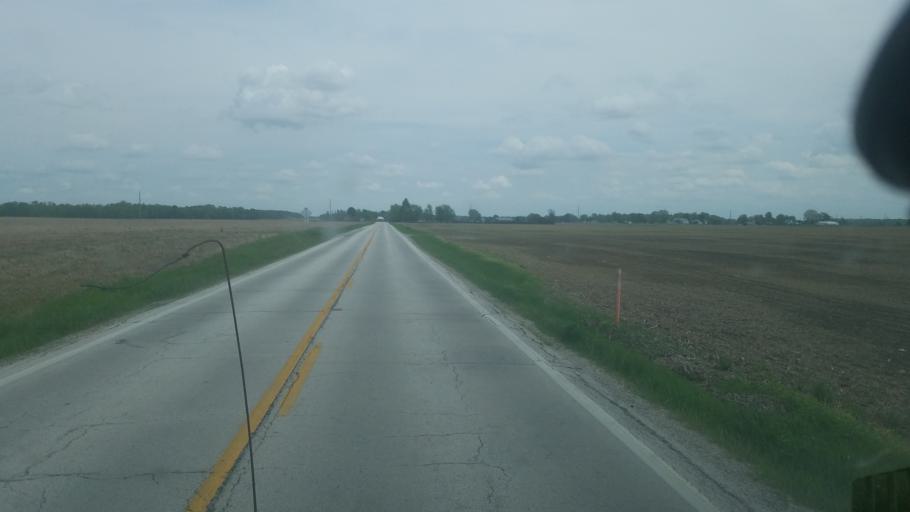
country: US
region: Ohio
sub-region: Seneca County
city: Tiffin
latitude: 41.0616
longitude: -83.1397
